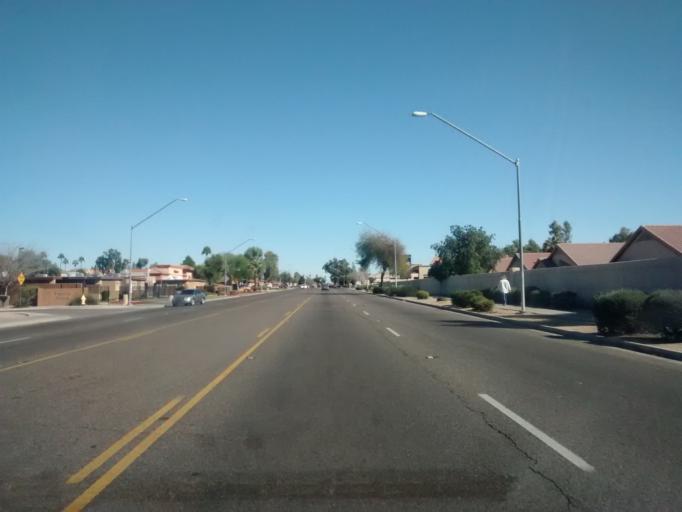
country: US
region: Arizona
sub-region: Maricopa County
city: Glendale
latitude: 33.5237
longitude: -112.2069
